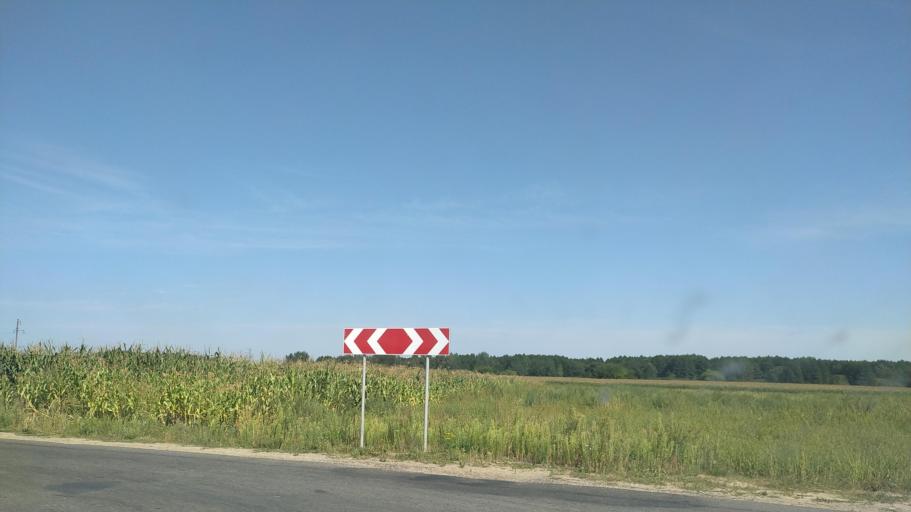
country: BY
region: Brest
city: Byaroza
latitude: 52.5209
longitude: 24.9894
